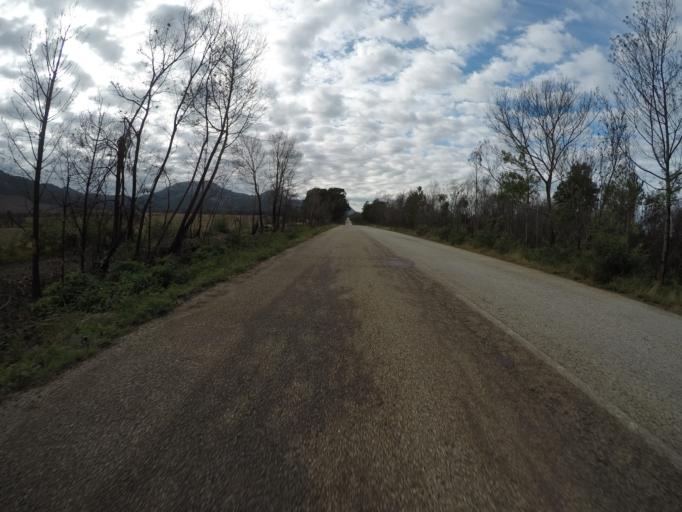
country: ZA
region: Eastern Cape
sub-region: Cacadu District Municipality
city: Kareedouw
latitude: -34.0151
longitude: 24.3229
